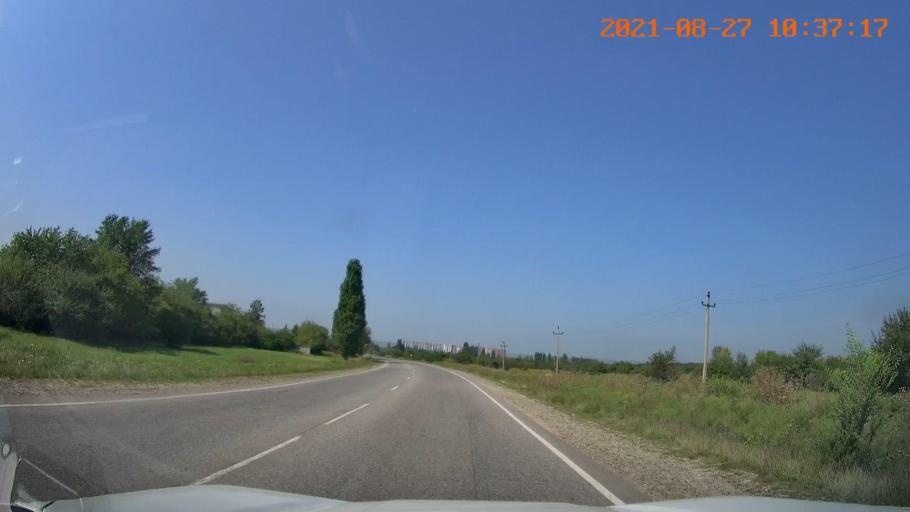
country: RU
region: Karachayevo-Cherkesiya
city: Cherkessk
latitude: 44.2545
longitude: 42.0801
